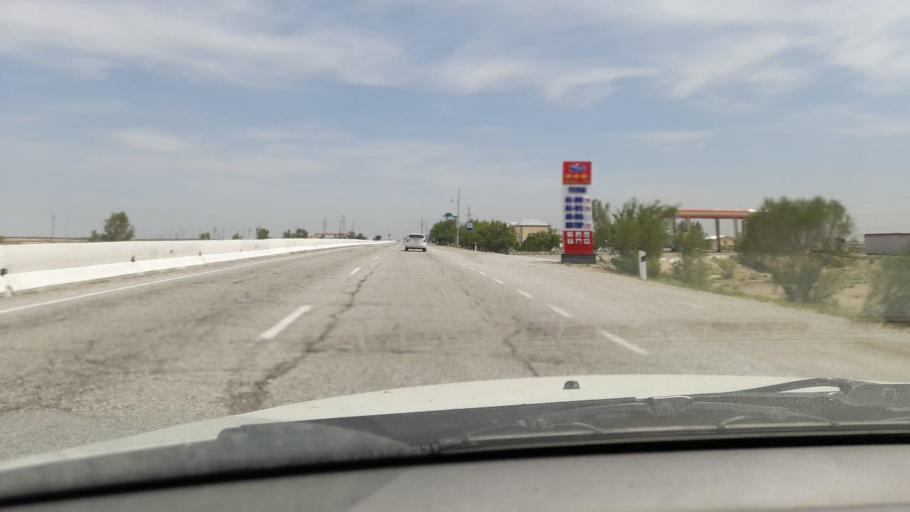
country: UZ
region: Navoiy
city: Qiziltepa
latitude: 40.0927
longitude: 64.9756
